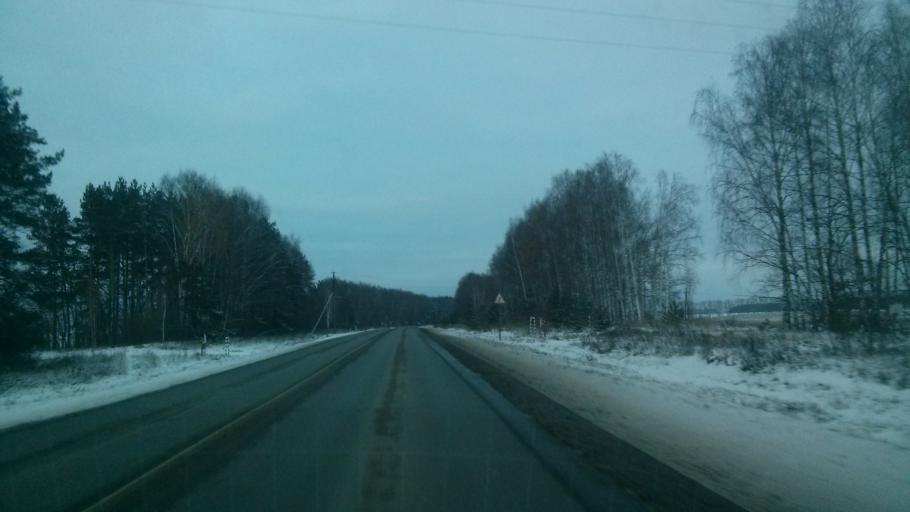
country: RU
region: Nizjnij Novgorod
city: Vorsma
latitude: 56.0447
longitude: 43.3889
